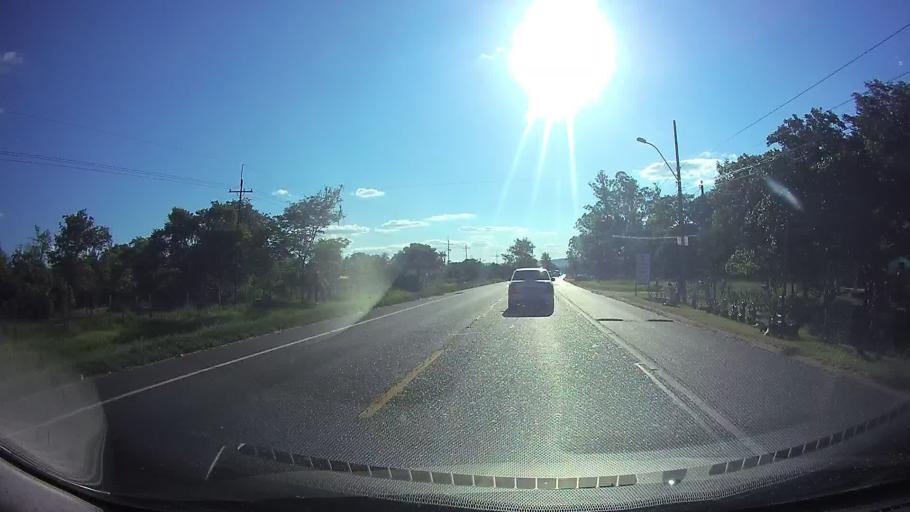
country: PY
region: Central
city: Ypacarai
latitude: -25.3784
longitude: -57.2384
